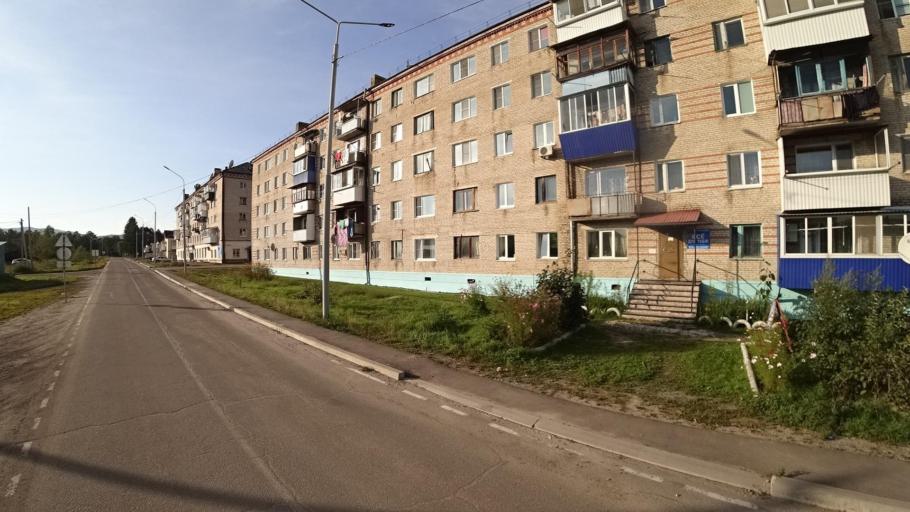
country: RU
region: Jewish Autonomous Oblast
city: Kul'dur
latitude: 49.2021
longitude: 131.6240
